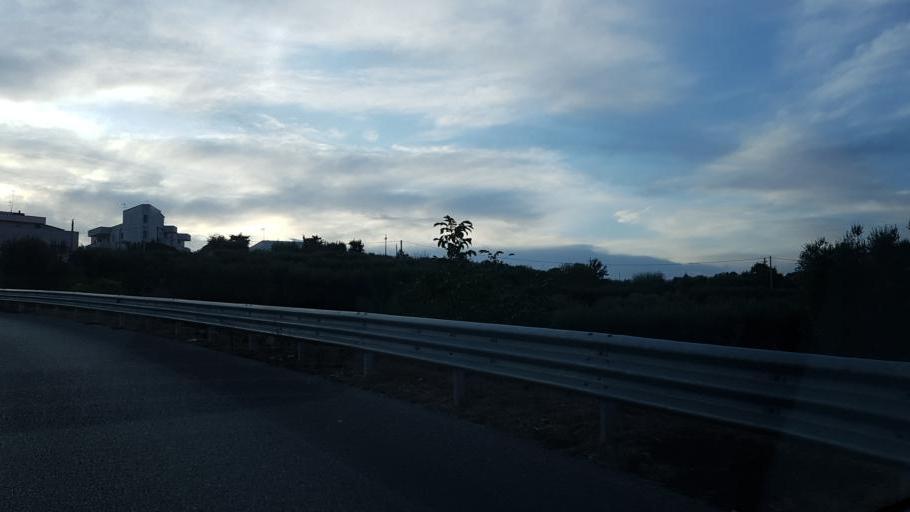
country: IT
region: Apulia
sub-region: Provincia di Bari
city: Locorotondo
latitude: 40.7646
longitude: 17.3234
